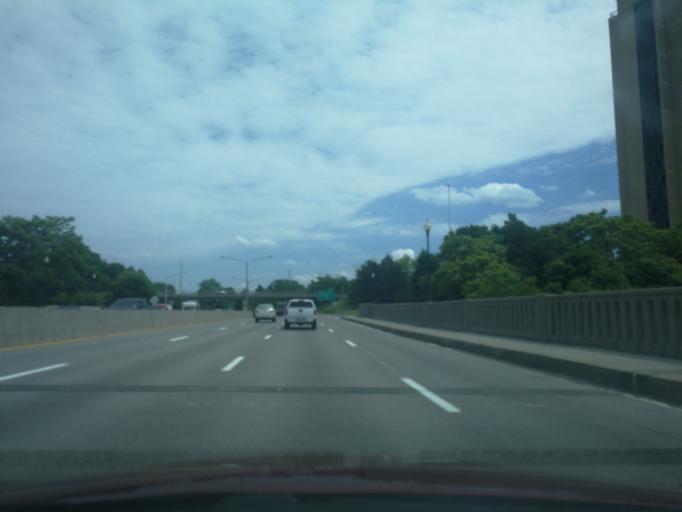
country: US
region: New York
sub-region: Monroe County
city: Rochester
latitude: 43.1922
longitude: -77.6198
